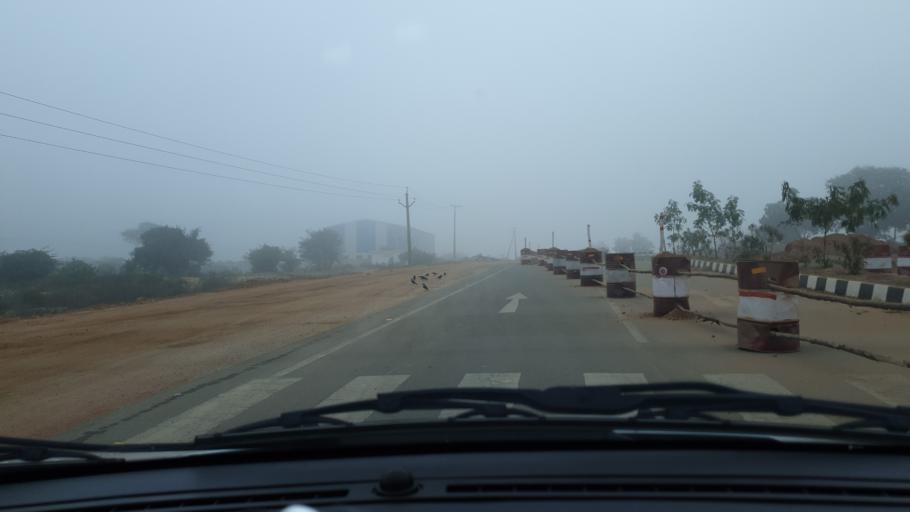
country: IN
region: Telangana
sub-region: Mahbubnagar
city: Nagar Karnul
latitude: 16.6615
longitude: 78.5764
